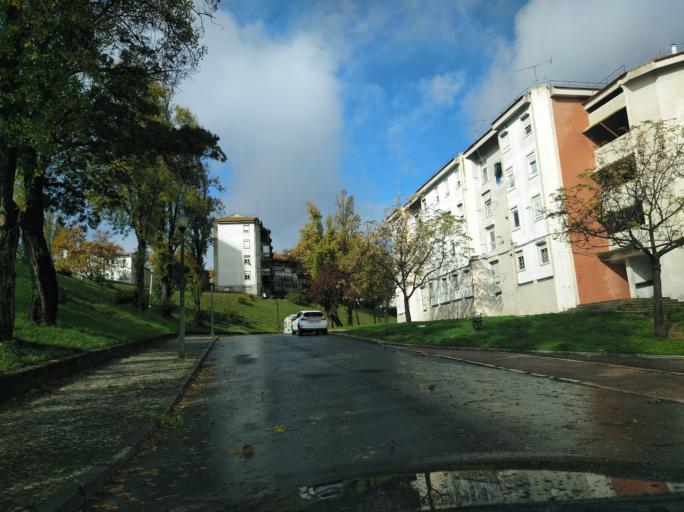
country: PT
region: Lisbon
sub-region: Loures
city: Moscavide
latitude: 38.7592
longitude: -9.1063
